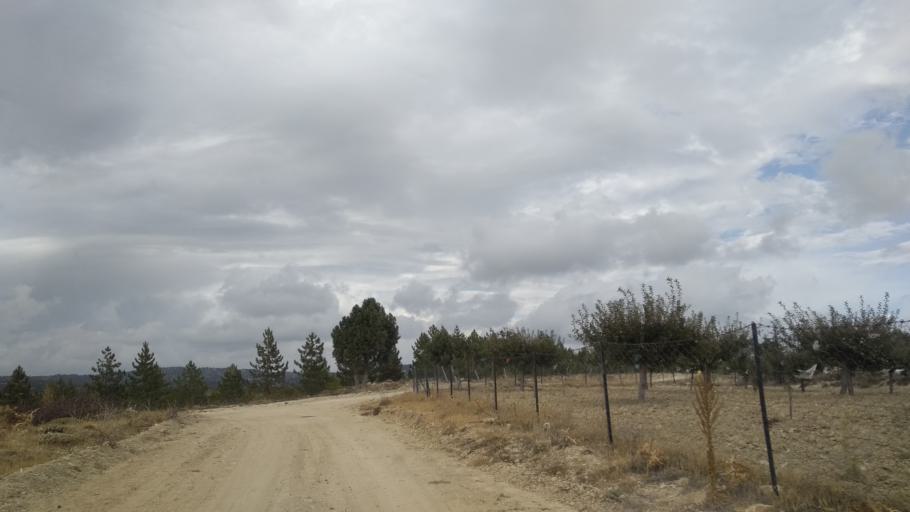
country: TR
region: Mersin
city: Sarikavak
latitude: 36.5740
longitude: 33.7572
